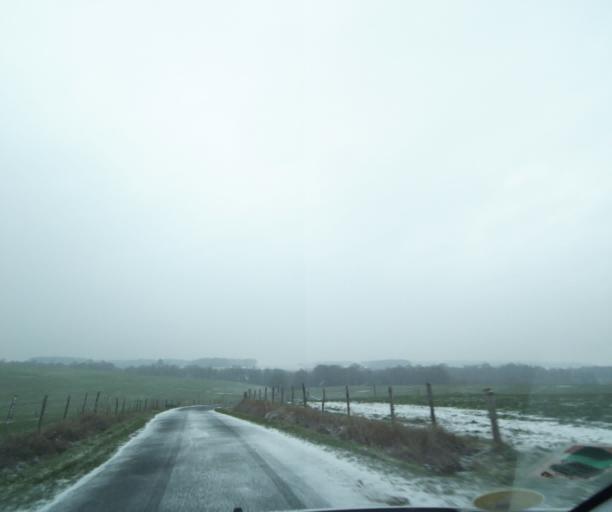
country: FR
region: Champagne-Ardenne
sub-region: Departement de la Haute-Marne
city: Wassy
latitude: 48.4785
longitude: 5.0398
